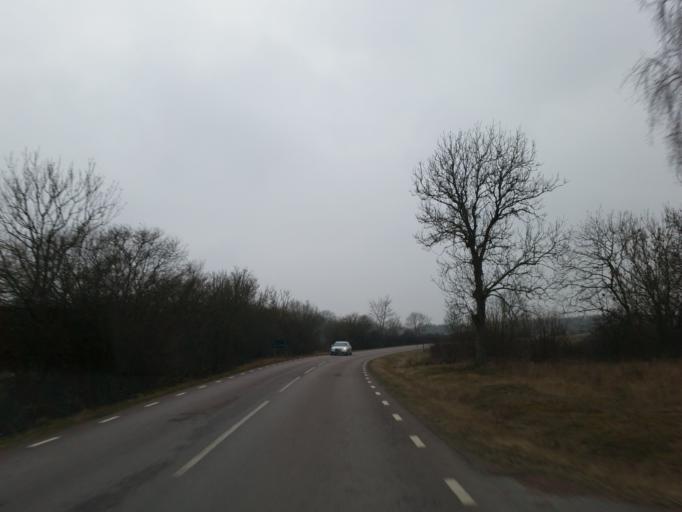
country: SE
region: Kalmar
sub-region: Morbylanga Kommun
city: Sodra Sandby
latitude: 56.6505
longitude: 16.5678
